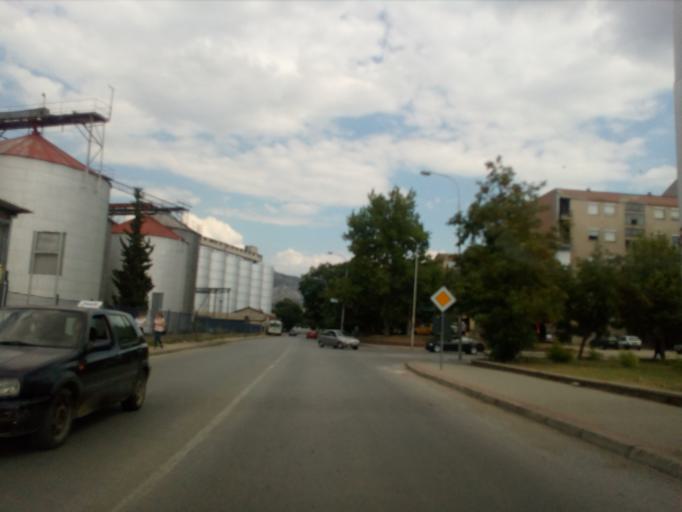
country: MK
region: Veles
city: Veles
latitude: 41.7200
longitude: 21.7682
